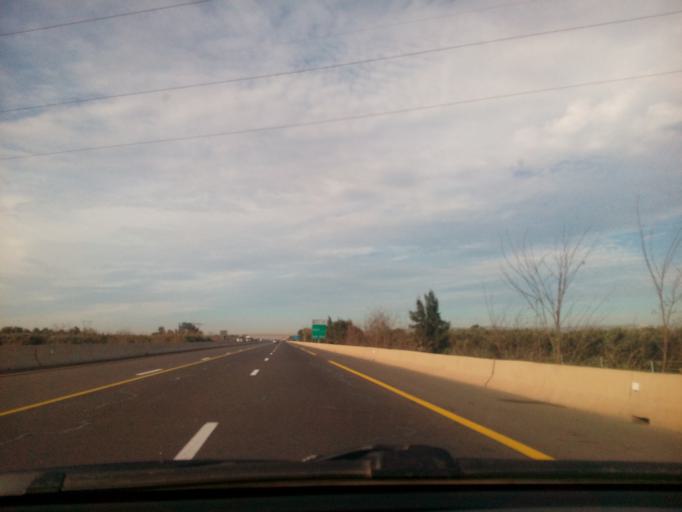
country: DZ
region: Mascara
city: Sig
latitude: 35.5814
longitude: -0.2326
